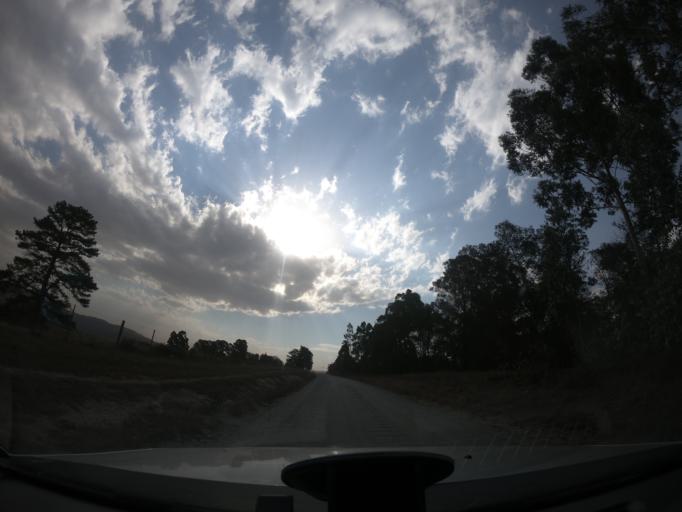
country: ZA
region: KwaZulu-Natal
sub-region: uMgungundlovu District Municipality
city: Howick
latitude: -29.4286
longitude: 30.1083
